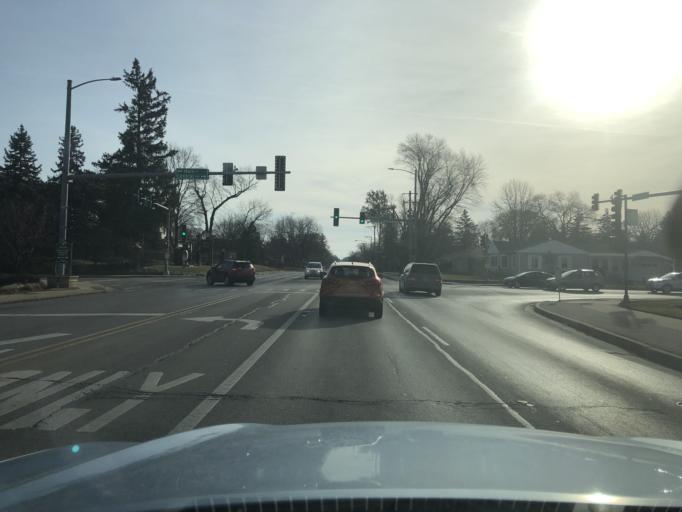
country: US
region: Illinois
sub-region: DuPage County
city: Roselle
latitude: 41.9840
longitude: -88.0803
